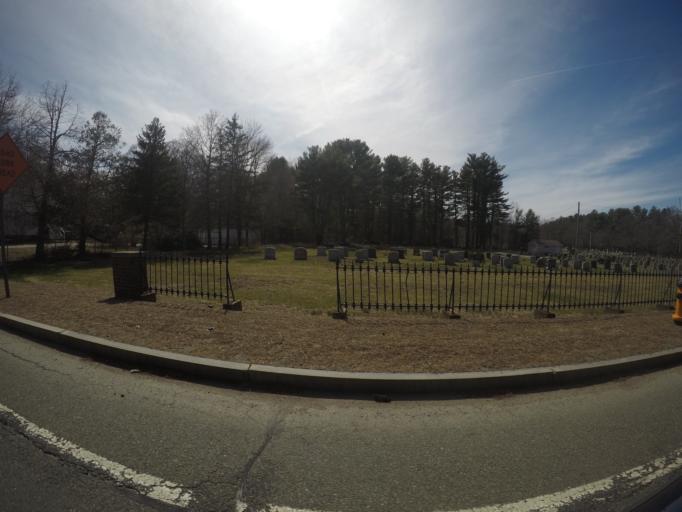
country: US
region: Massachusetts
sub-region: Bristol County
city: Easton
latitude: 42.0547
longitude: -71.0856
